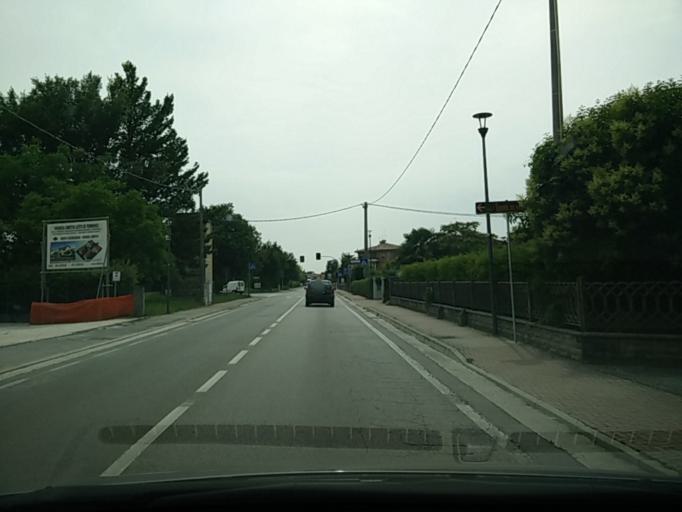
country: IT
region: Veneto
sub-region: Provincia di Treviso
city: Roncade
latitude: 45.6319
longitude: 12.3818
